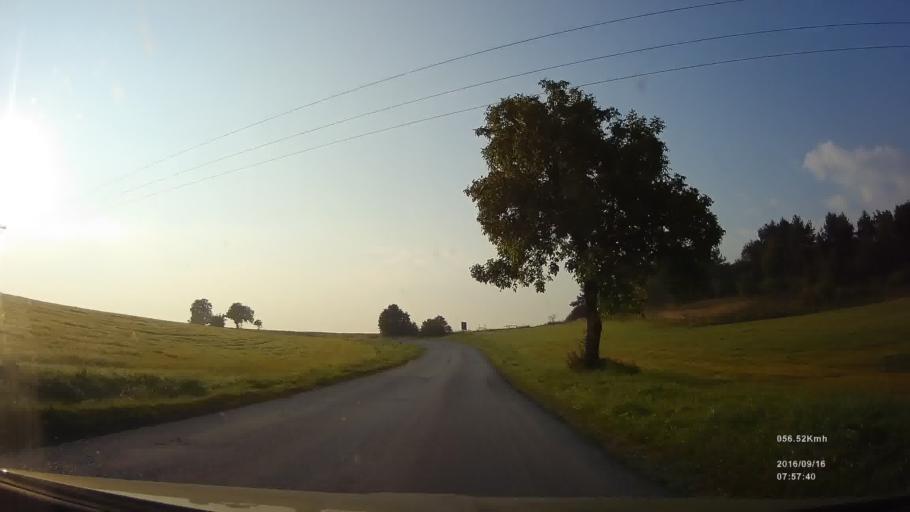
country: SK
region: Presovsky
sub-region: Okres Presov
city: Presov
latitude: 48.9130
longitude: 21.1464
